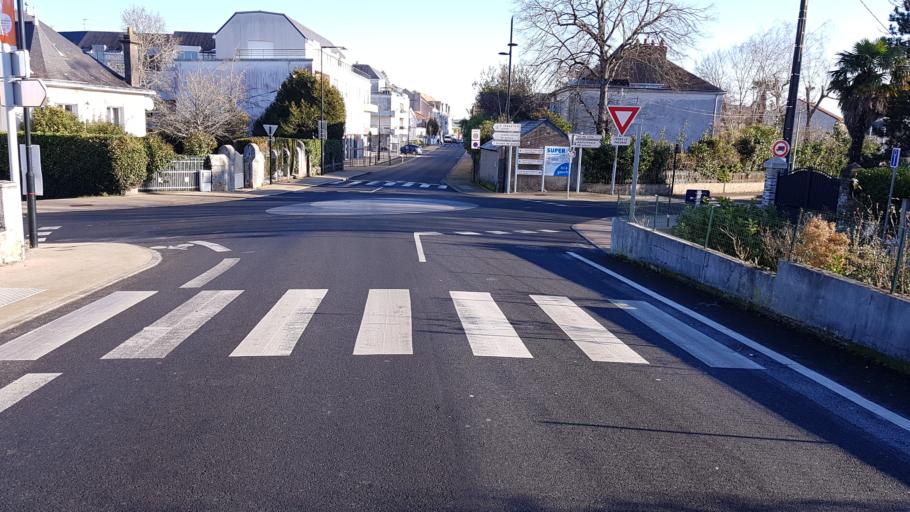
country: FR
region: Pays de la Loire
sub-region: Departement de la Loire-Atlantique
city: Saint-Sebastien-sur-Loire
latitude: 47.2057
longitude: -1.5092
